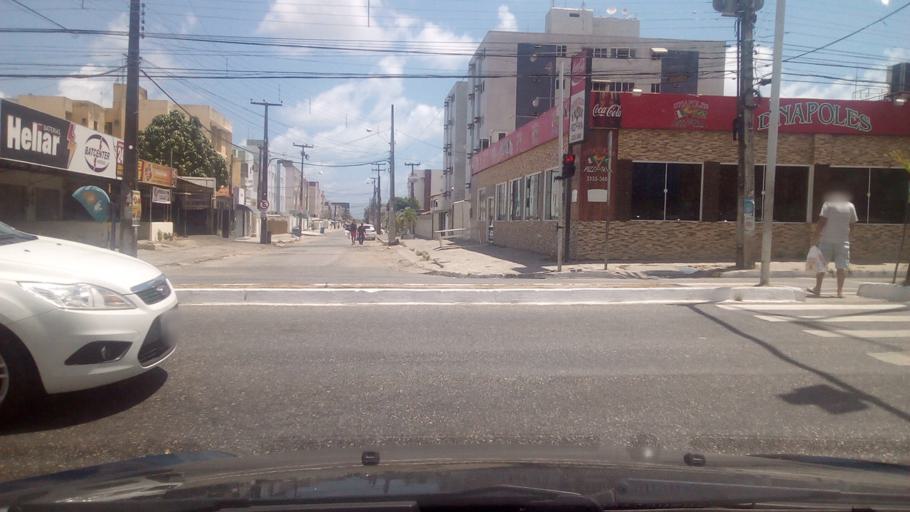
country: BR
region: Paraiba
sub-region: Joao Pessoa
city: Joao Pessoa
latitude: -7.1584
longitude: -34.8386
